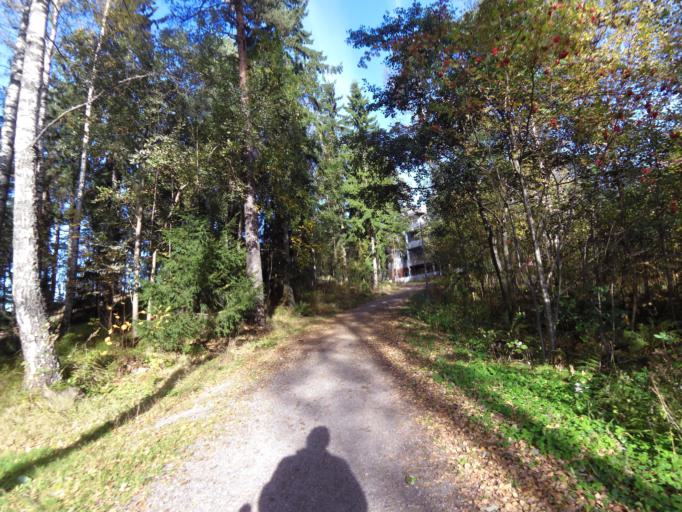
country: FI
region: Uusimaa
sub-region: Helsinki
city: Espoo
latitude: 60.1482
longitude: 24.6350
